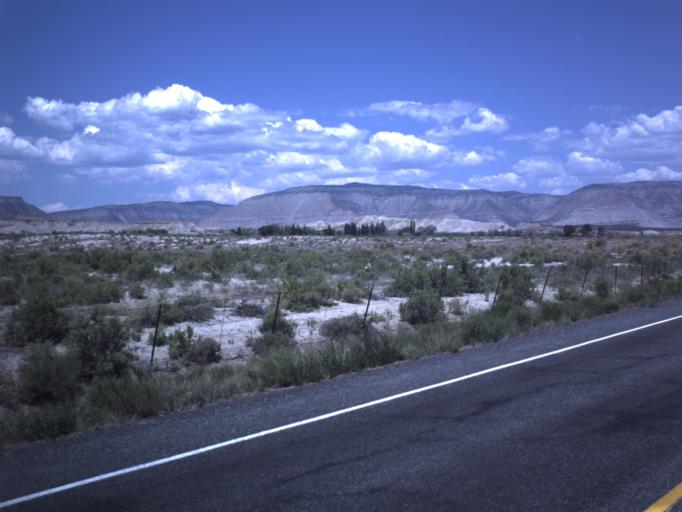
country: US
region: Utah
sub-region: Emery County
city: Orangeville
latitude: 39.2004
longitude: -111.0479
